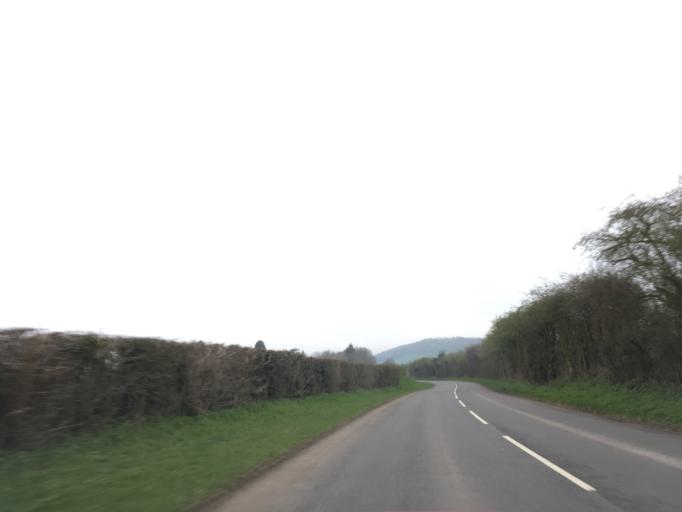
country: GB
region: Wales
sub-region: Monmouthshire
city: Usk
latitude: 51.7169
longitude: -2.9131
